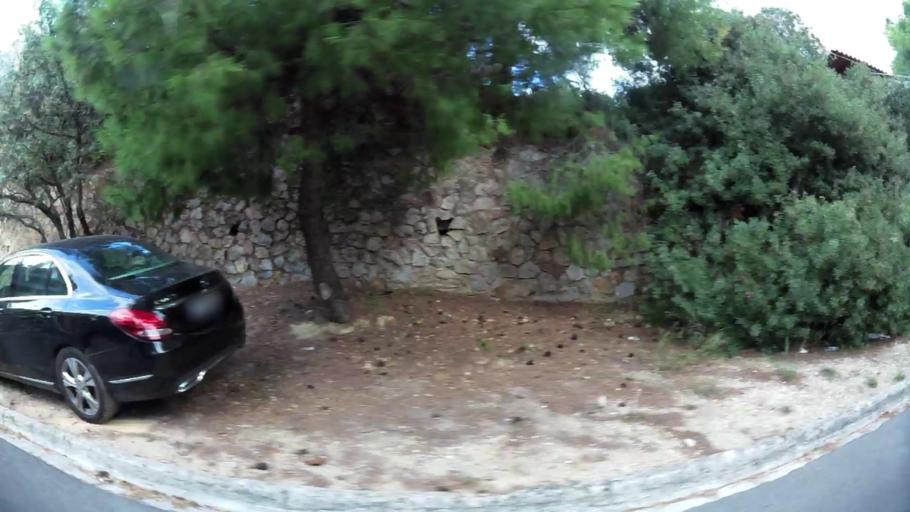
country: GR
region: Attica
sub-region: Nomarchia Athinas
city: Melissia
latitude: 38.0593
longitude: 23.8280
